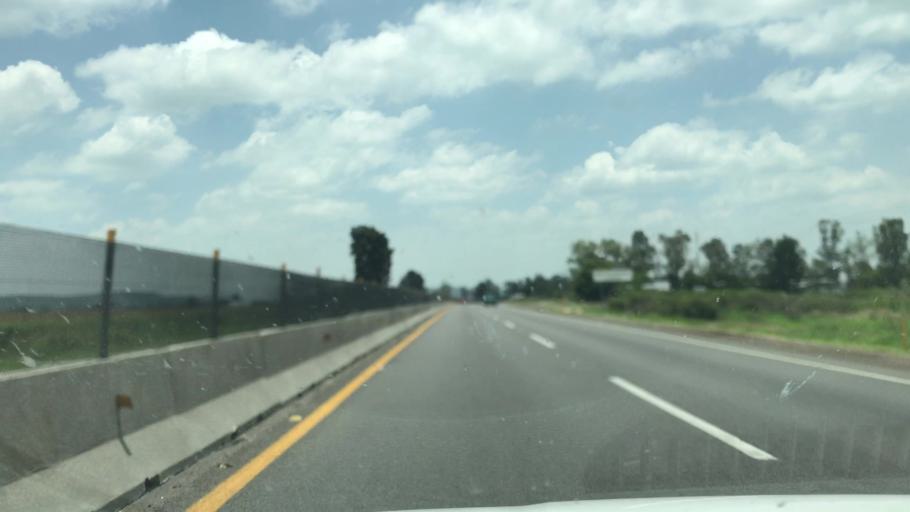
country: MX
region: Guanajuato
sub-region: Abasolo
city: San Bernardo Pena Blanca
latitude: 20.4963
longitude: -101.4829
